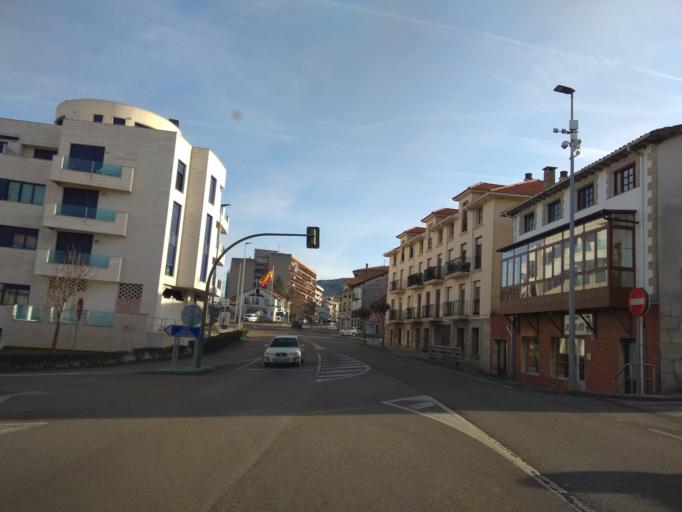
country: ES
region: Cantabria
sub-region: Provincia de Cantabria
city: El Astillero
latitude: 43.4012
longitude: -3.8266
